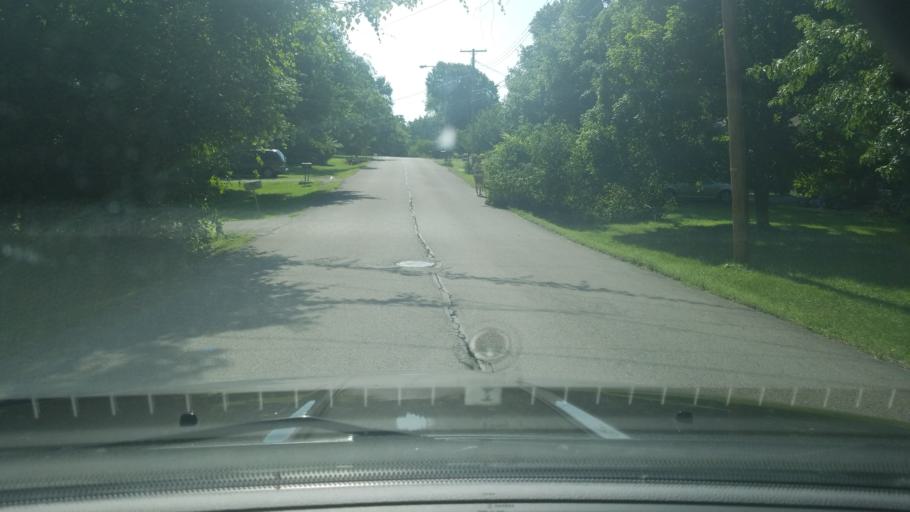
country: US
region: Tennessee
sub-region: Davidson County
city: Oak Hill
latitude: 36.1084
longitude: -86.7388
